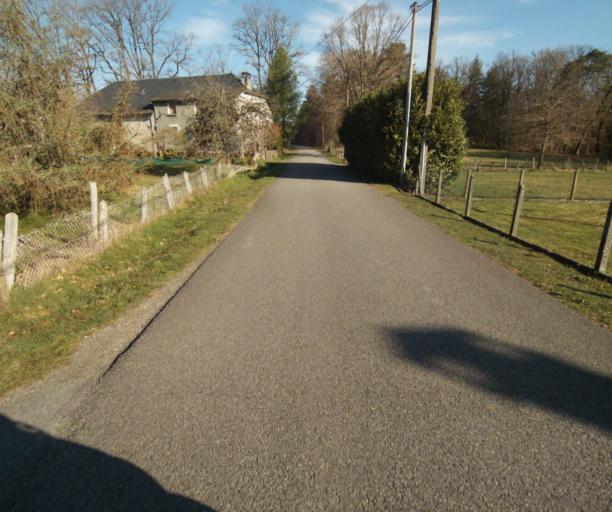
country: FR
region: Limousin
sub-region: Departement de la Correze
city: Correze
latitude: 45.3240
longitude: 1.8849
